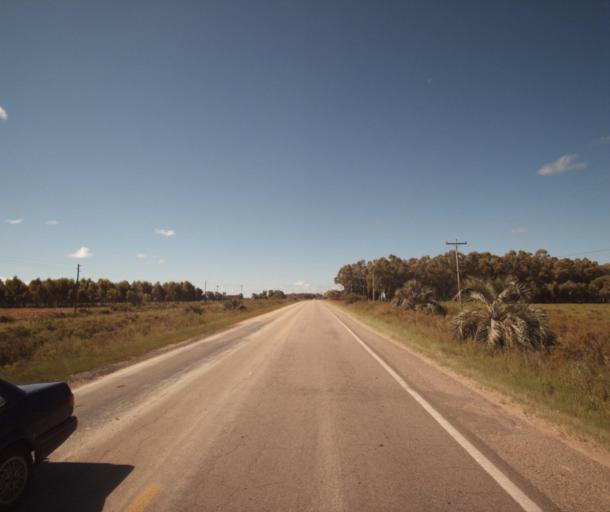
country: BR
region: Rio Grande do Sul
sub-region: Santa Vitoria Do Palmar
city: Santa Vitoria do Palmar
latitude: -33.5648
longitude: -53.3728
